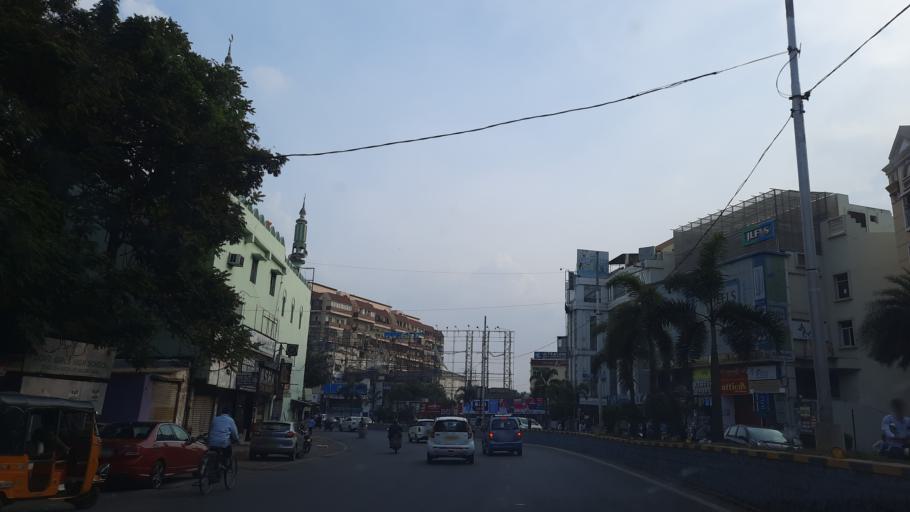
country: IN
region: Telangana
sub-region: Hyderabad
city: Hyderabad
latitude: 17.4051
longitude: 78.4516
